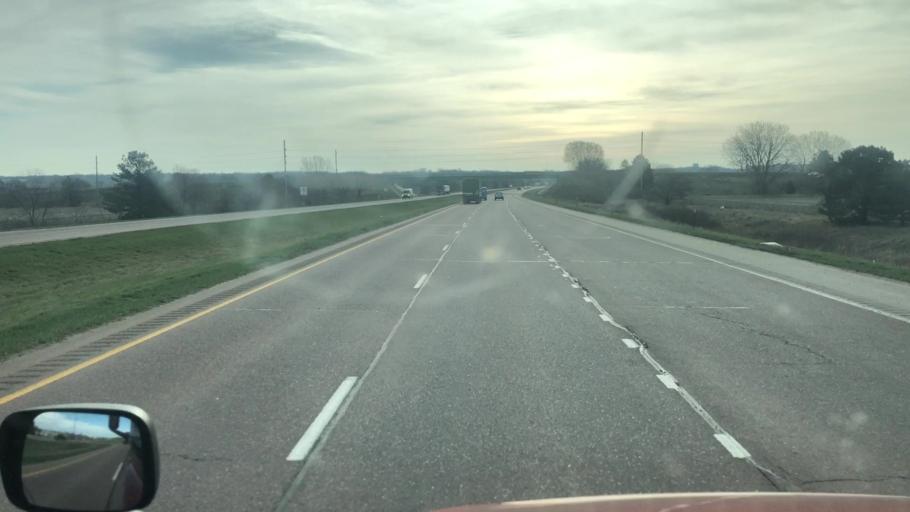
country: US
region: Nebraska
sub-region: Dakota County
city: South Sioux City
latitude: 42.4493
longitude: -96.4078
